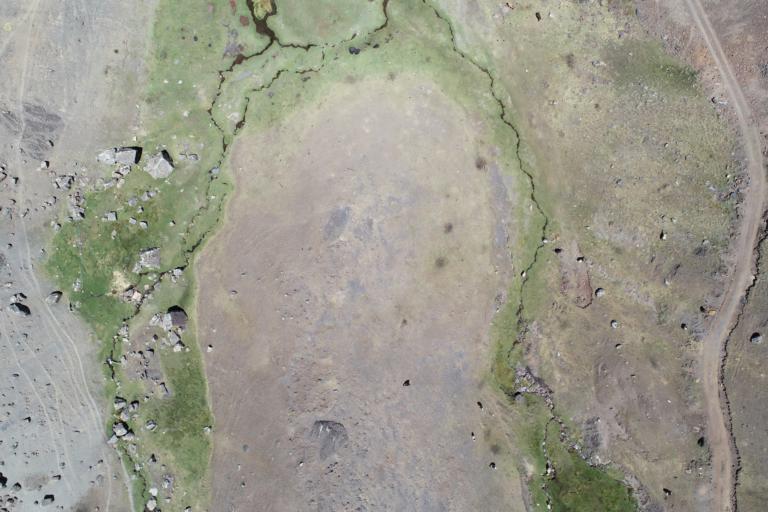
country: BO
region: La Paz
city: La Paz
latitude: -16.6205
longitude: -67.8273
